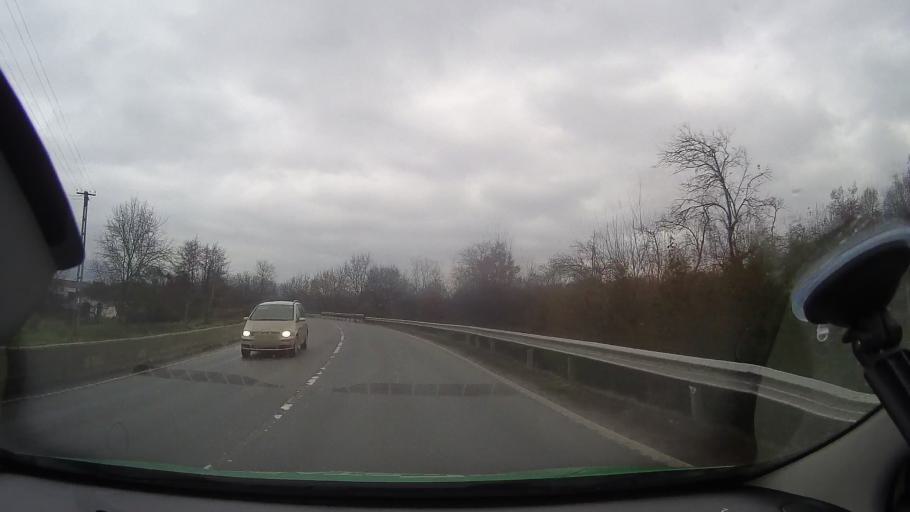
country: RO
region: Arad
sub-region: Comuna Gurahont
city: Gurahont
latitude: 46.2729
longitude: 22.3092
